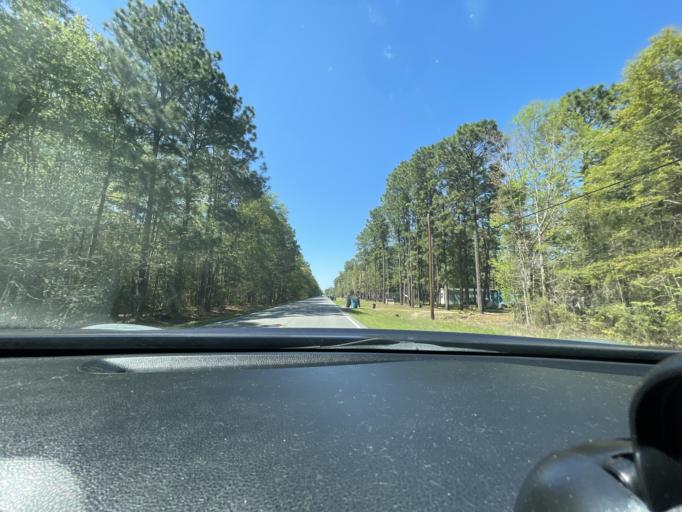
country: US
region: Georgia
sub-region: Chatham County
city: Bloomingdale
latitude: 32.1014
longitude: -81.3031
